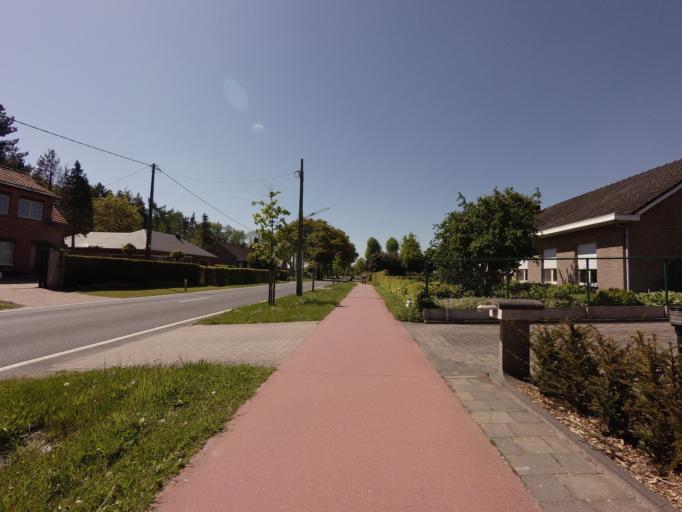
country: BE
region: Flanders
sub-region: Provincie Antwerpen
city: Essen
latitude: 51.4542
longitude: 4.4333
